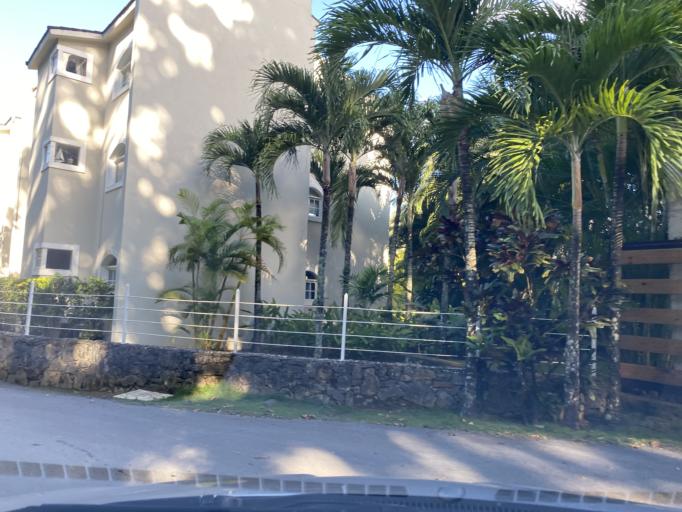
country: DO
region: Samana
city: Las Terrenas
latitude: 19.3175
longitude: -69.5594
